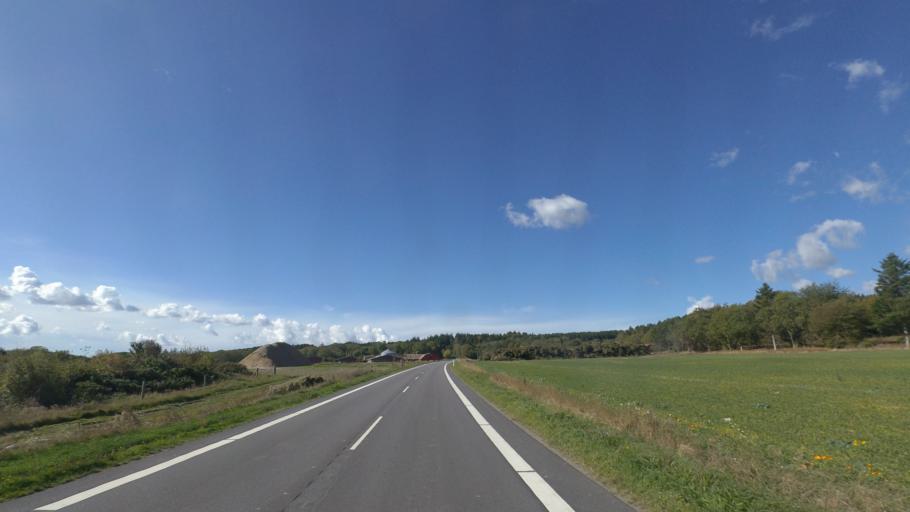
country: DK
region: Capital Region
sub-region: Bornholm Kommune
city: Nexo
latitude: 55.0632
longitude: 15.0263
